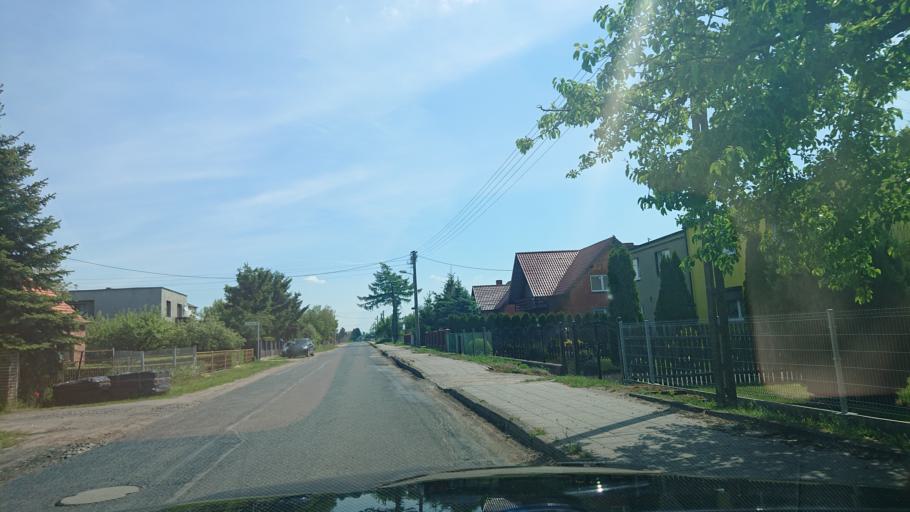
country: PL
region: Greater Poland Voivodeship
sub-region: Powiat gnieznienski
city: Gniezno
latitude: 52.4542
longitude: 17.5957
